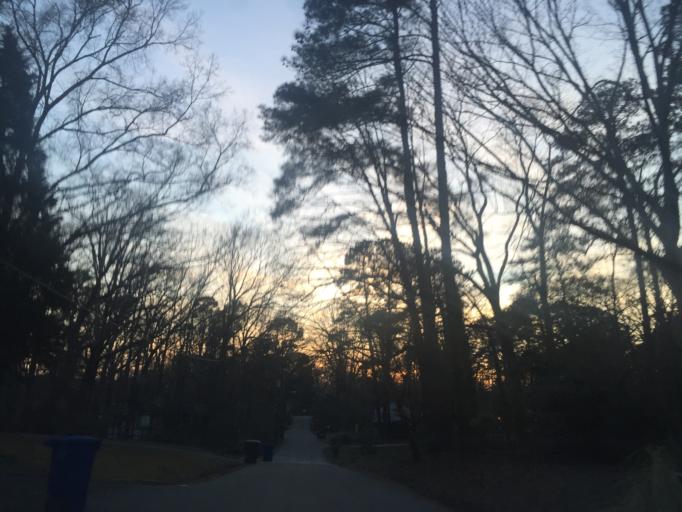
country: US
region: Virginia
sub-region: City of Newport News
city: Newport News
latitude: 37.0718
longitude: -76.5068
